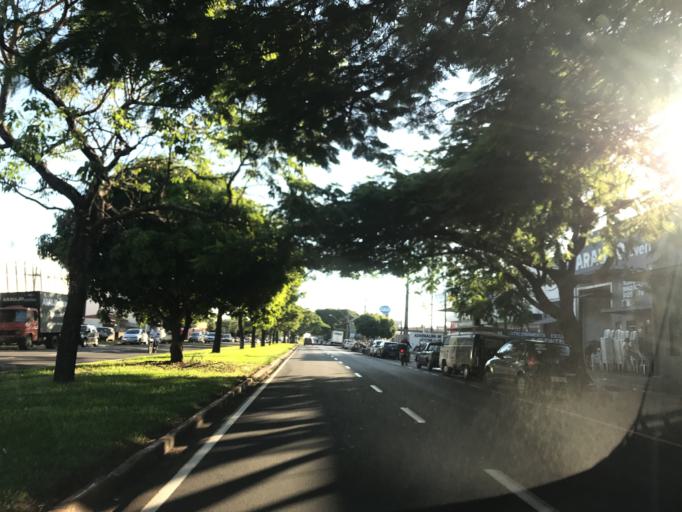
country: BR
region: Parana
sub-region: Maringa
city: Maringa
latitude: -23.4490
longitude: -51.9513
